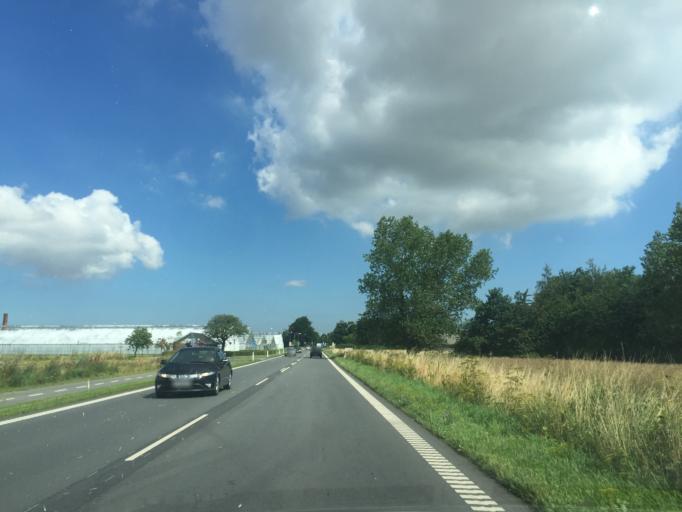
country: DK
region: South Denmark
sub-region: Nordfyns Kommune
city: Otterup
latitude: 55.4994
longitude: 10.3881
